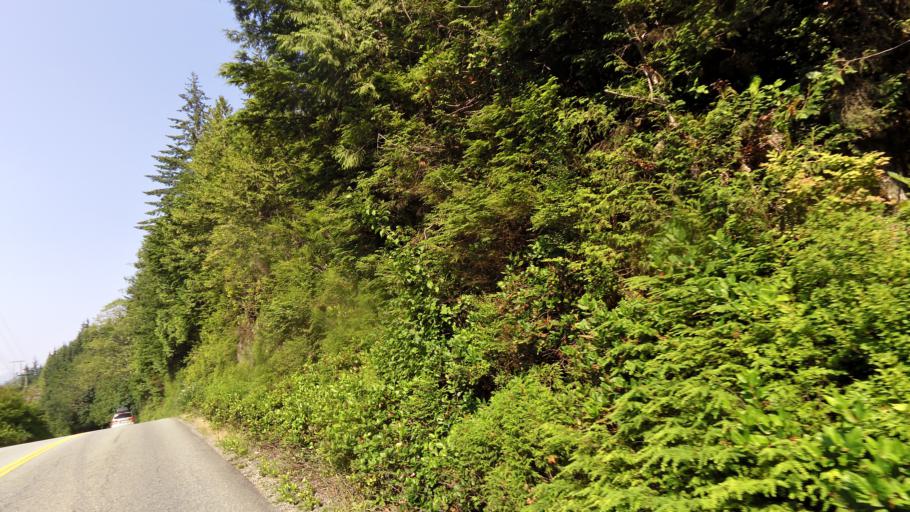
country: CA
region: British Columbia
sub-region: Regional District of Alberni-Clayoquot
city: Ucluelet
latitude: 49.0919
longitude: -125.4527
